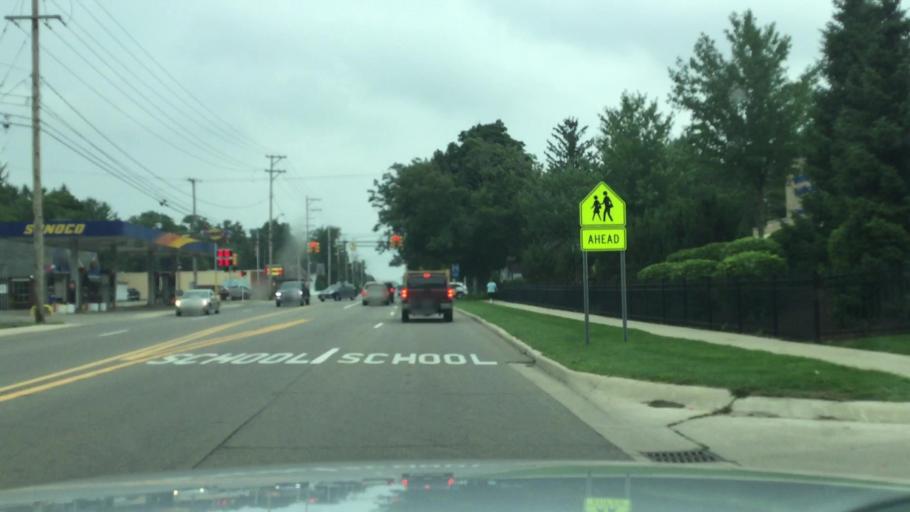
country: US
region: Michigan
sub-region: Shiawassee County
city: Owosso
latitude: 43.0058
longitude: -84.1769
